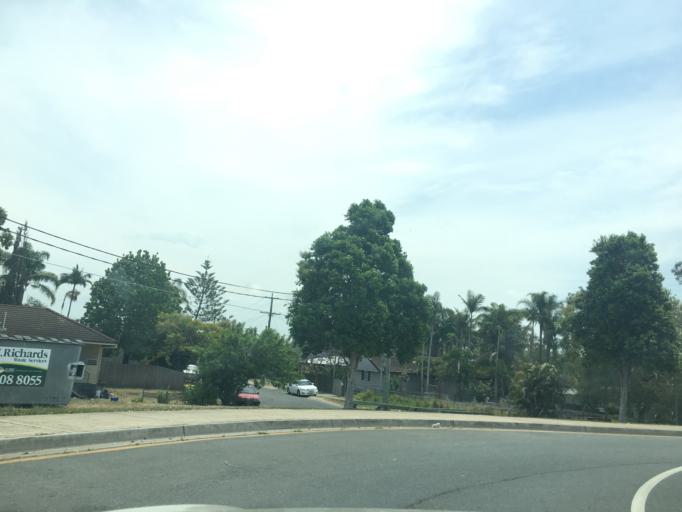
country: AU
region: Queensland
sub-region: Logan
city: Logan City
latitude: -27.6447
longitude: 153.1025
